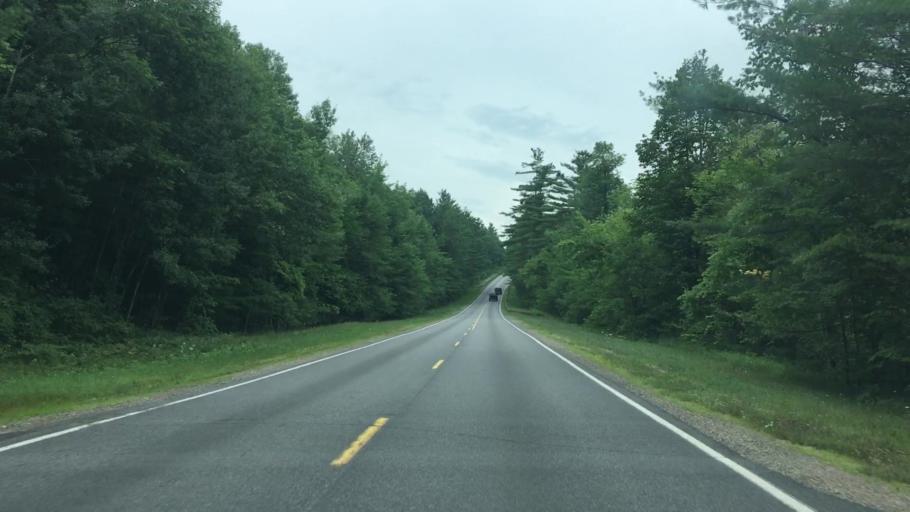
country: US
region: New York
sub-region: Clinton County
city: Peru
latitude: 44.4943
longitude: -73.5927
